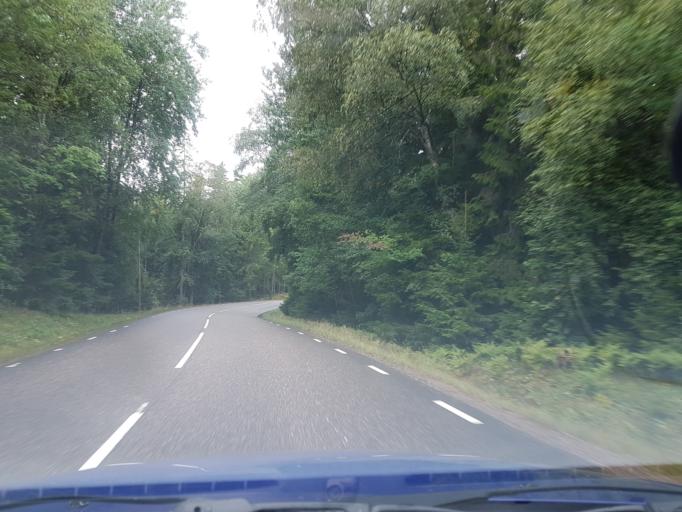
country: SE
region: Vaestra Goetaland
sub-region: Lerums Kommun
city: Grabo
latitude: 57.9184
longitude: 12.3209
